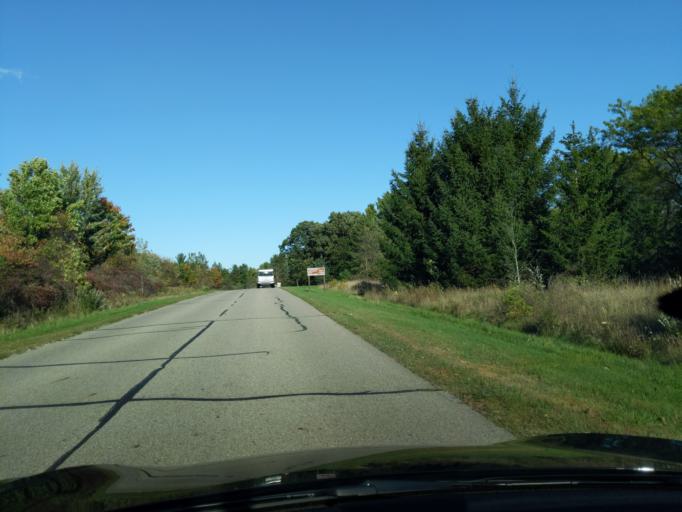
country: US
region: Michigan
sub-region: Shiawassee County
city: Laingsburg
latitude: 42.9295
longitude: -84.4070
